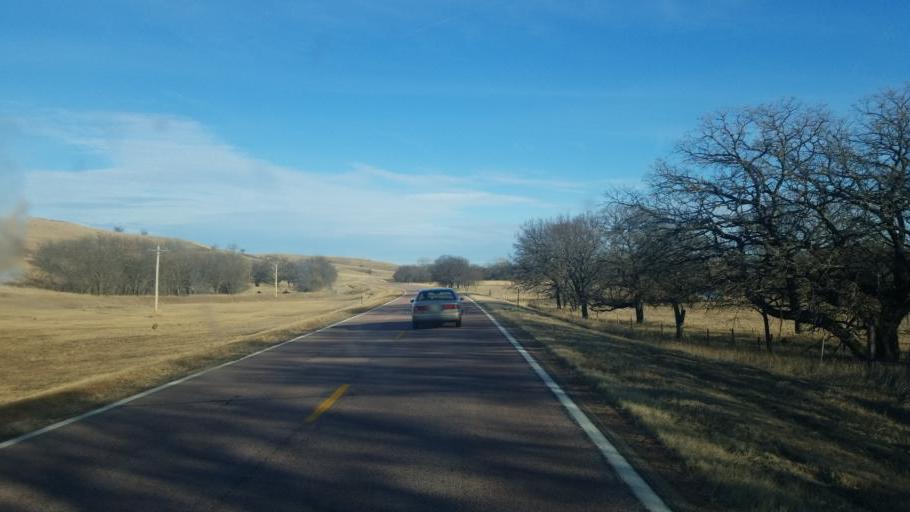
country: US
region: South Dakota
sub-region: Charles Mix County
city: Wagner
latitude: 42.8302
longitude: -98.3927
